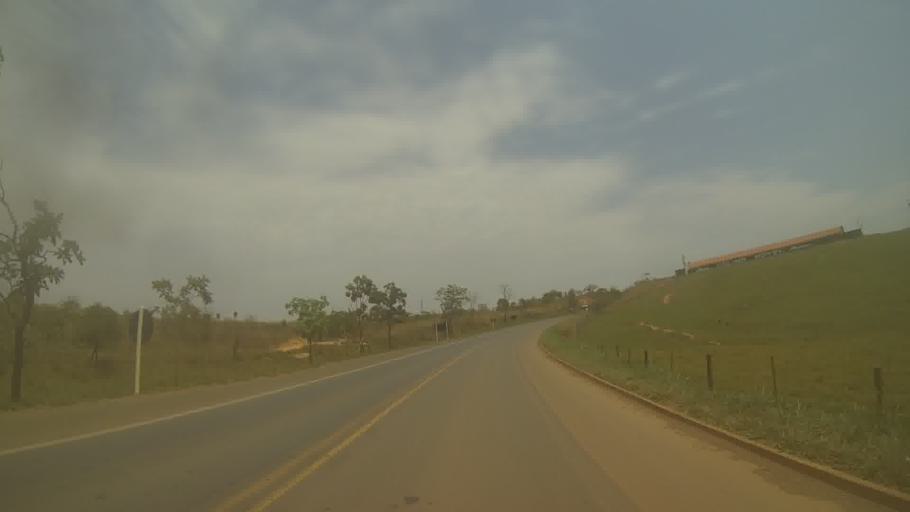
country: BR
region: Minas Gerais
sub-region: Bambui
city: Bambui
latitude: -20.0158
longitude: -45.9397
